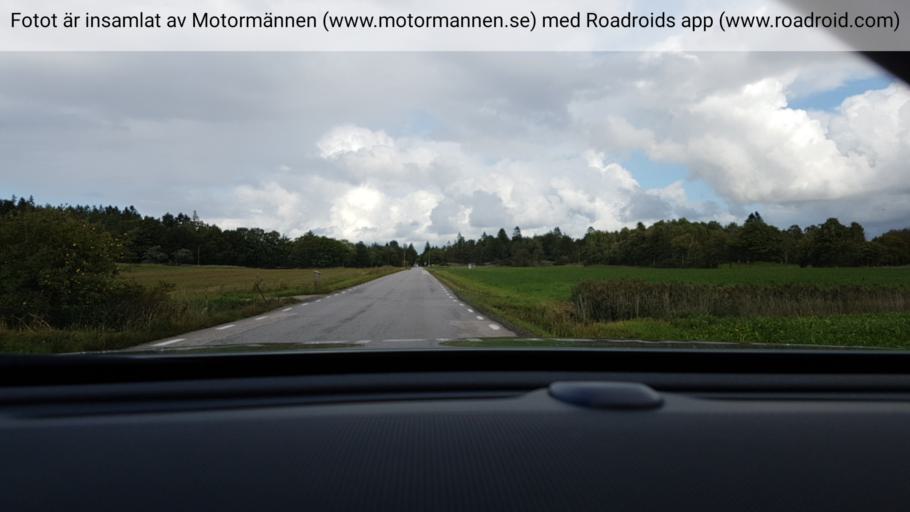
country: SE
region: Vaestra Goetaland
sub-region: Orust
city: Henan
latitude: 58.1739
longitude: 11.6017
